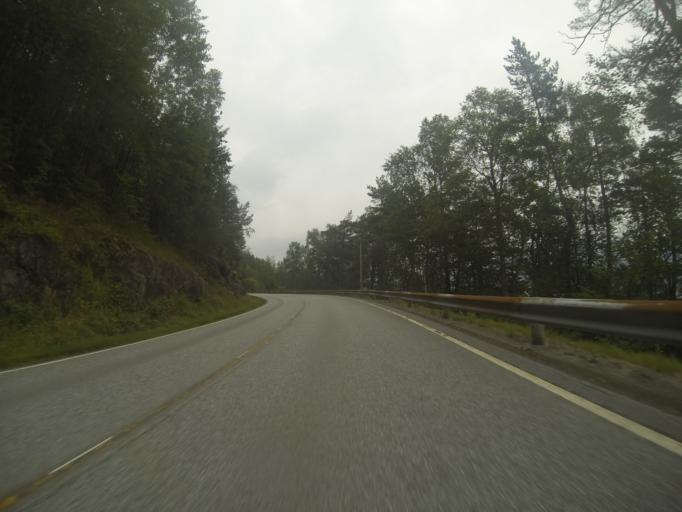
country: NO
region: Rogaland
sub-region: Suldal
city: Sand
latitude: 59.5122
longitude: 6.2232
